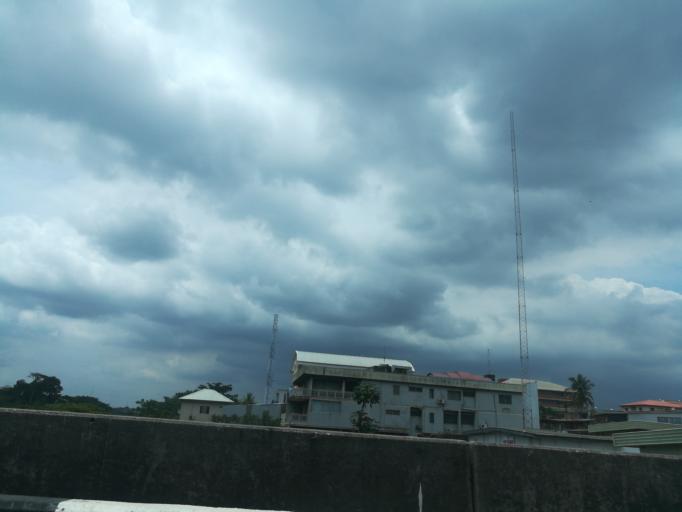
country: NG
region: Lagos
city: Ojota
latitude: 6.5858
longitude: 3.3635
